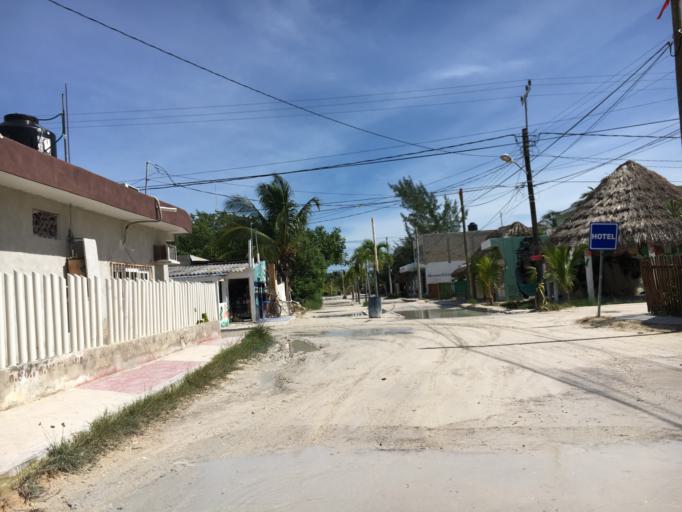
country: MX
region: Quintana Roo
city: Kantunilkin
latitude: 21.5226
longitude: -87.3774
